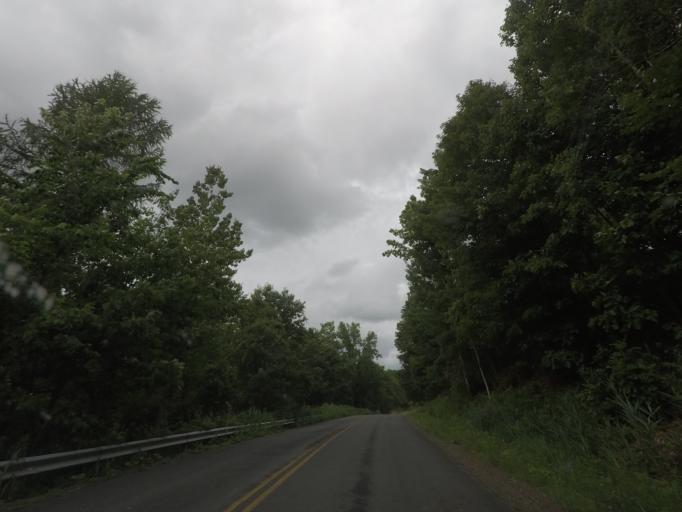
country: US
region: New York
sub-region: Rensselaer County
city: West Sand Lake
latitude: 42.6501
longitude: -73.6302
